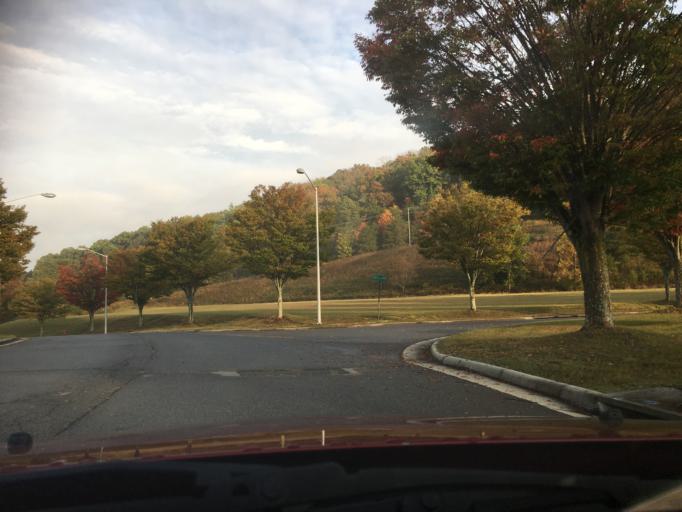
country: US
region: Virginia
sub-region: City of Radford
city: Radford
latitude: 37.0958
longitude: -80.5753
